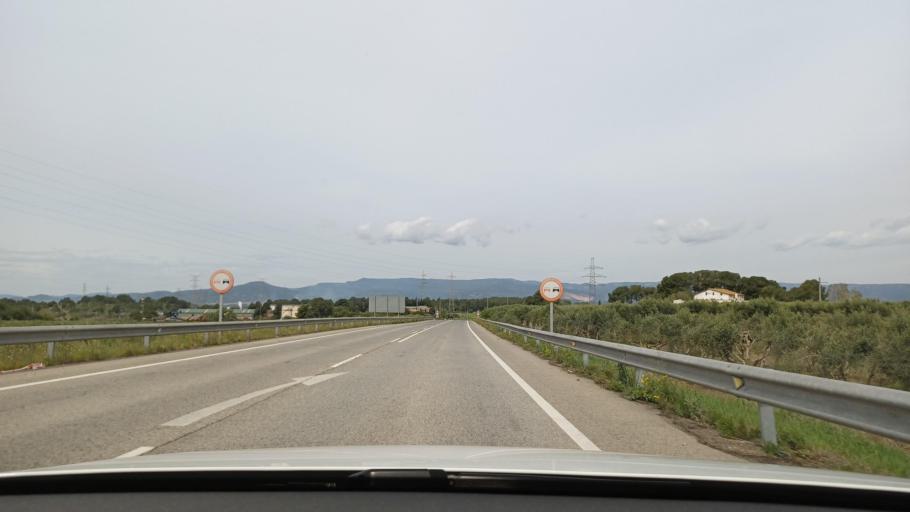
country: ES
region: Catalonia
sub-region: Provincia de Tarragona
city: La Secuita
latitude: 41.1994
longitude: 1.2492
